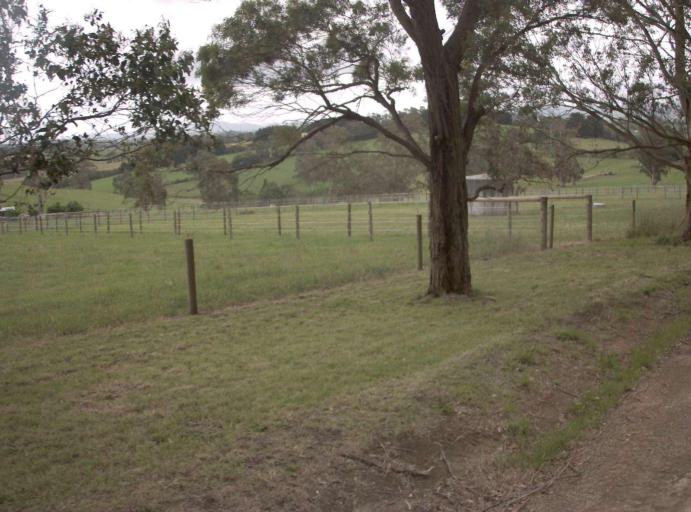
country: AU
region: Victoria
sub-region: Baw Baw
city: Warragul
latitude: -38.0951
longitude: 145.9687
